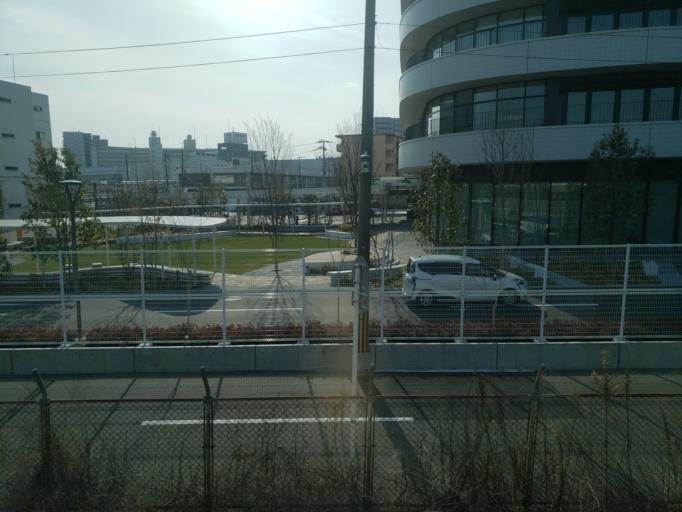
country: JP
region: Hyogo
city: Amagasaki
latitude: 34.7198
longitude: 135.4626
